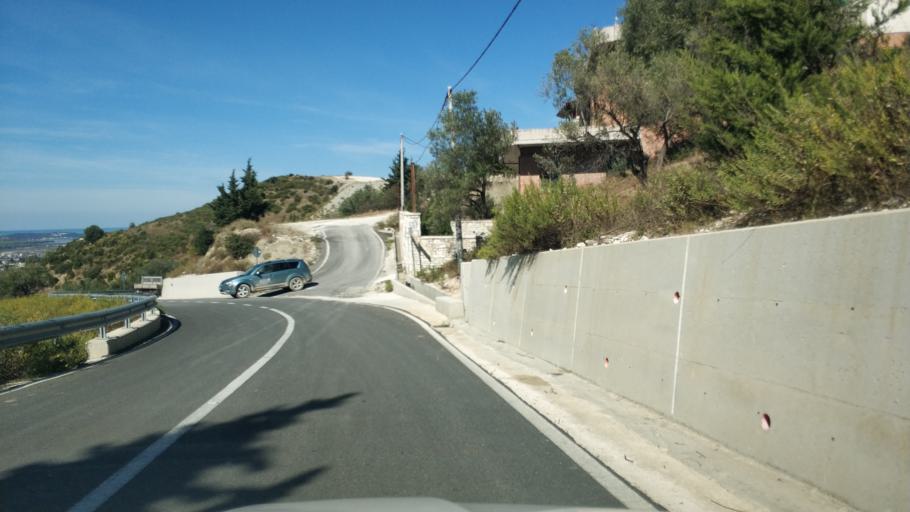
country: AL
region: Vlore
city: Vlore
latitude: 40.4553
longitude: 19.5148
